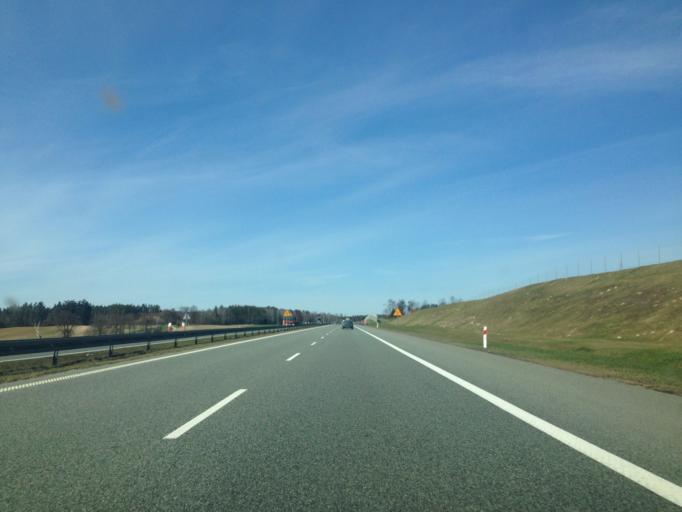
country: PL
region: Pomeranian Voivodeship
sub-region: Powiat starogardzki
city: Bobowo
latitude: 53.8686
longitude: 18.6294
